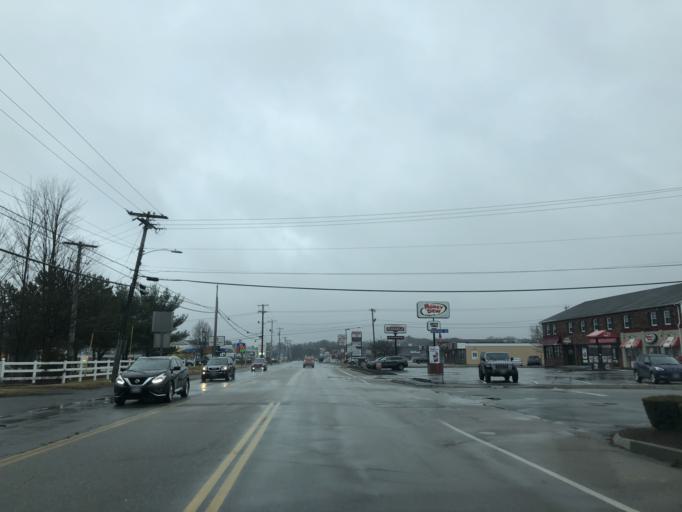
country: US
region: Massachusetts
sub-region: Norfolk County
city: Plainville
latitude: 42.0094
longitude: -71.3045
